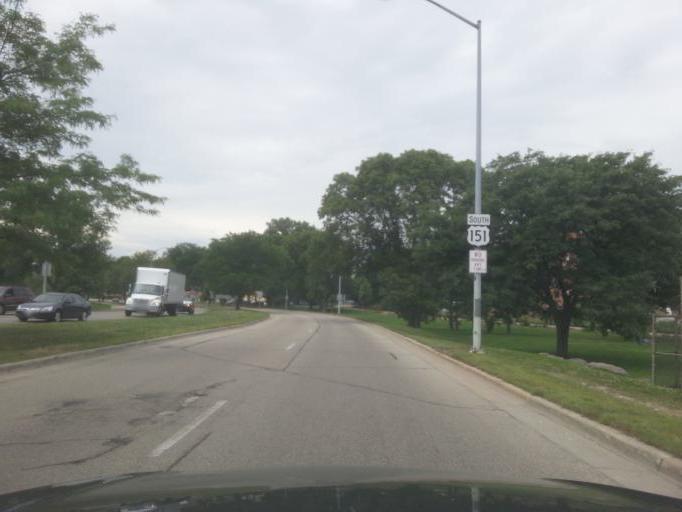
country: US
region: Wisconsin
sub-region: Dane County
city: Madison
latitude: 43.0672
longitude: -89.3861
